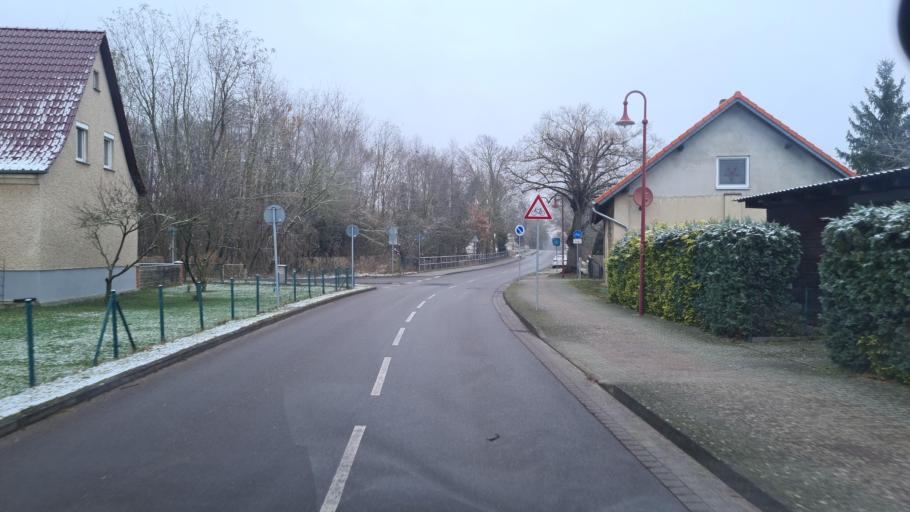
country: DE
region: Brandenburg
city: Storkow
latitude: 52.2551
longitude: 13.8940
